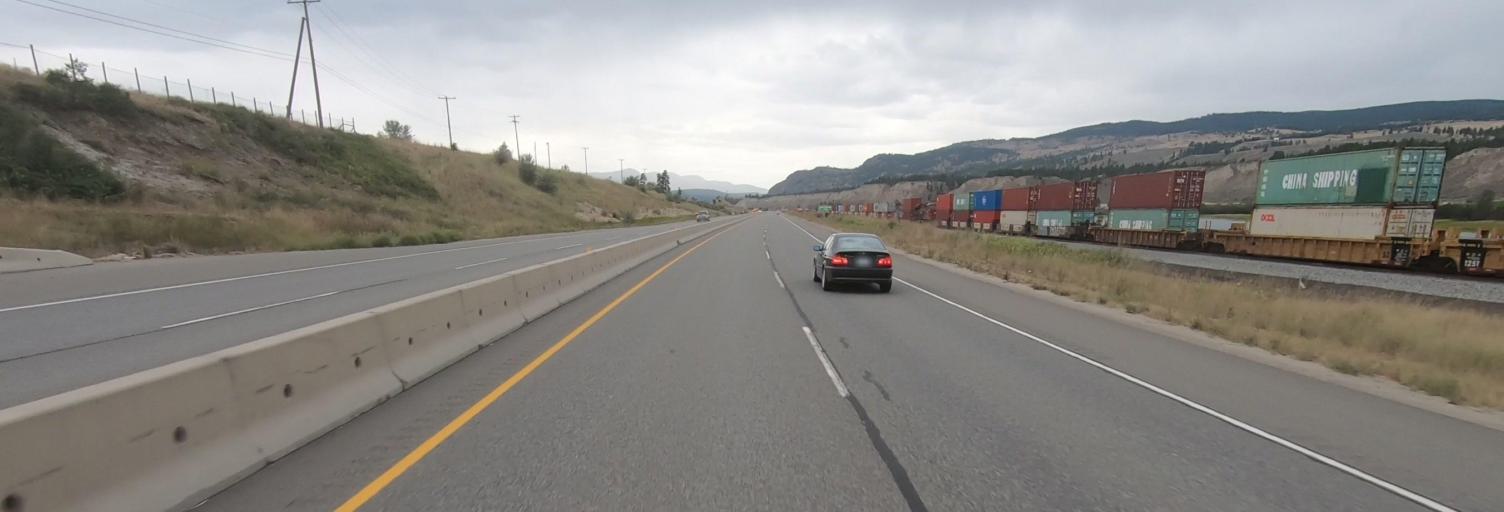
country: CA
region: British Columbia
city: Chase
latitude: 50.6734
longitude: -119.8384
